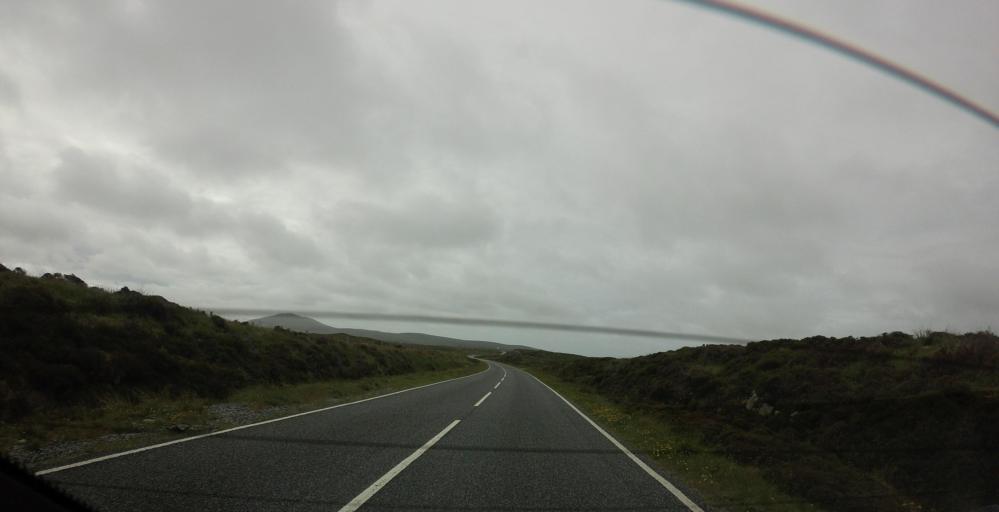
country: GB
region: Scotland
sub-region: Eilean Siar
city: Isle of South Uist
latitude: 57.2619
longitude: -7.3704
